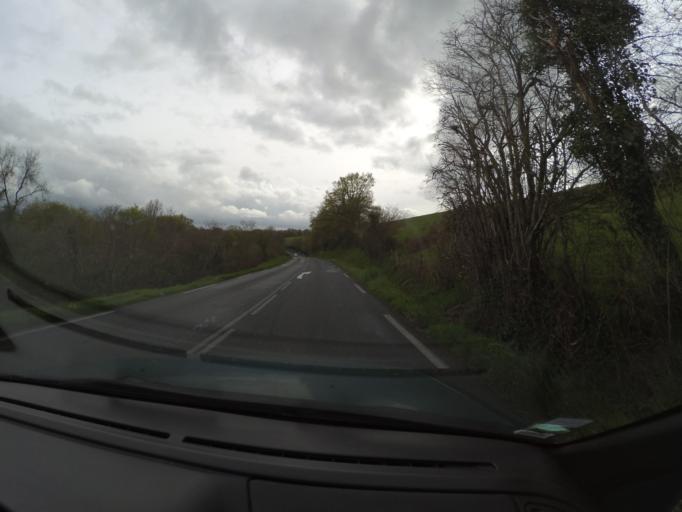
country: FR
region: Pays de la Loire
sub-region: Departement de Maine-et-Loire
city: Saint-Laurent-des-Autels
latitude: 47.3045
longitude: -1.1639
